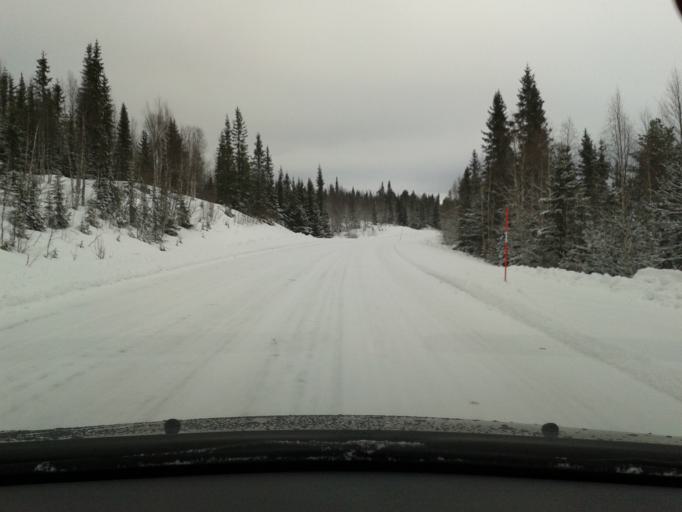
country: SE
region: Vaesterbotten
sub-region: Vilhelmina Kommun
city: Sjoberg
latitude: 65.2289
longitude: 15.8837
